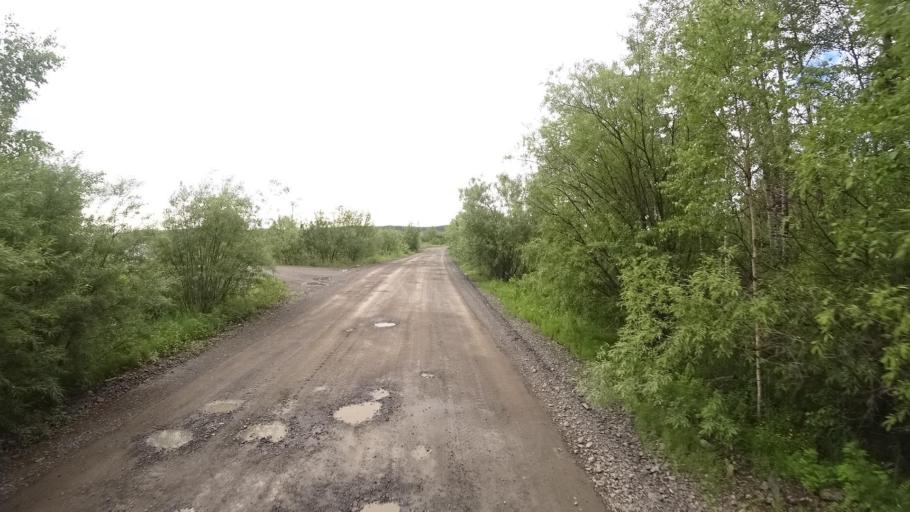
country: RU
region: Khabarovsk Krai
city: Amursk
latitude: 49.9061
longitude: 136.1423
